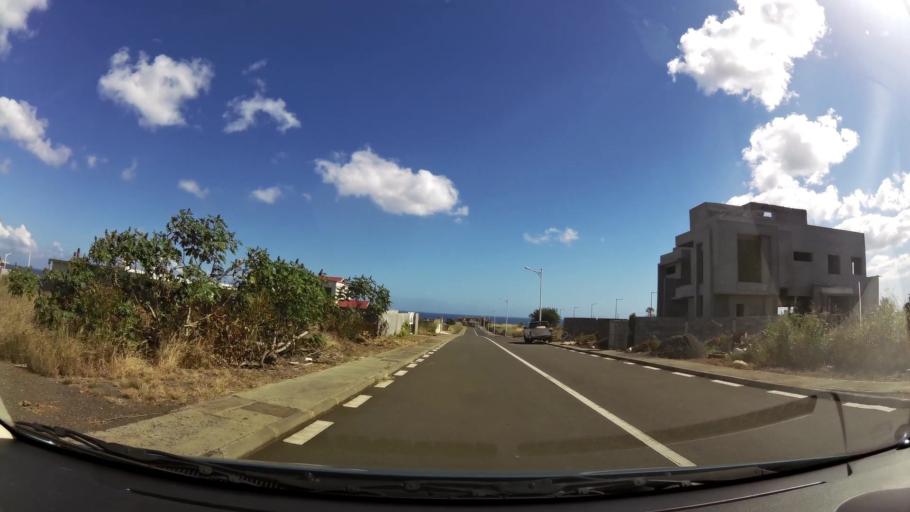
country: MU
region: Black River
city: Flic en Flac
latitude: -20.2779
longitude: 57.3853
